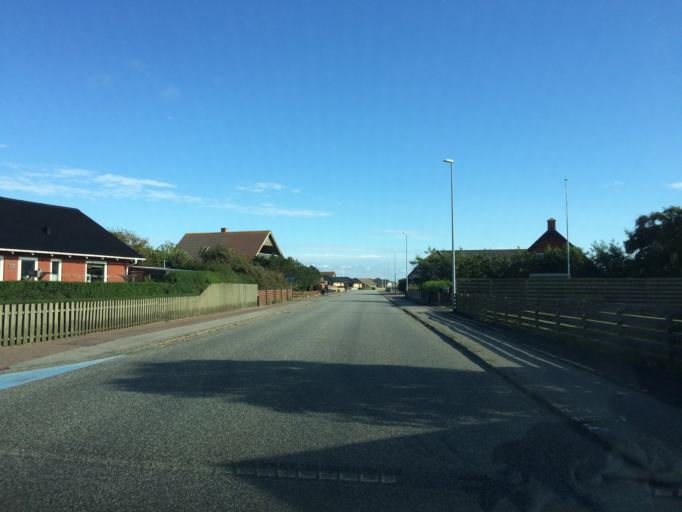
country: DK
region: Central Jutland
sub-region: Ringkobing-Skjern Kommune
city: Hvide Sande
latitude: 56.0149
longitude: 8.1255
